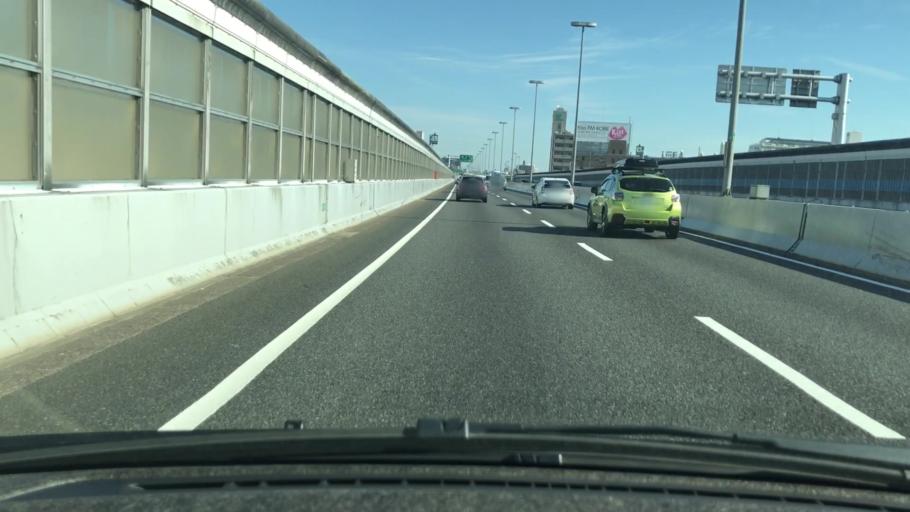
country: JP
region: Hyogo
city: Ashiya
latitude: 34.7150
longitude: 135.2803
